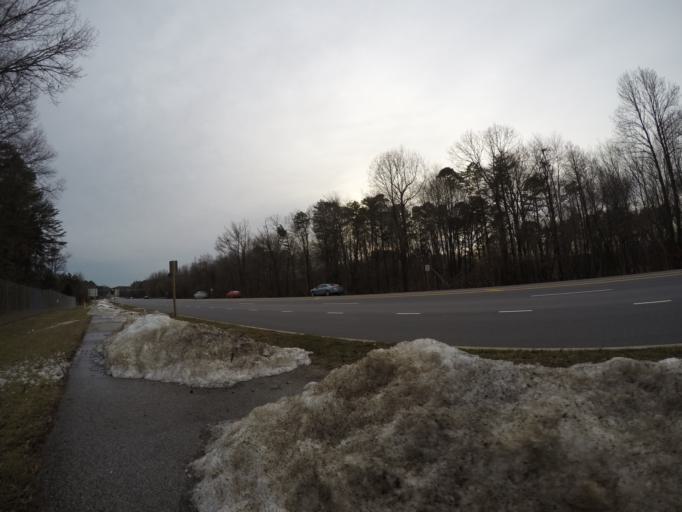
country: US
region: Maryland
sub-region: Anne Arundel County
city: Severn
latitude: 39.1725
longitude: -76.6939
